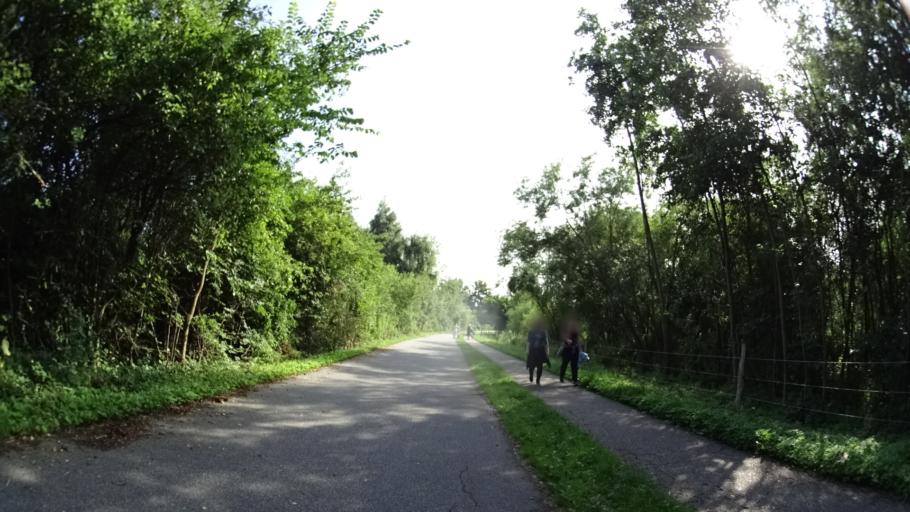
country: DK
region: Central Jutland
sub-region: Arhus Kommune
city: Arhus
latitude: 56.1499
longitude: 10.1783
